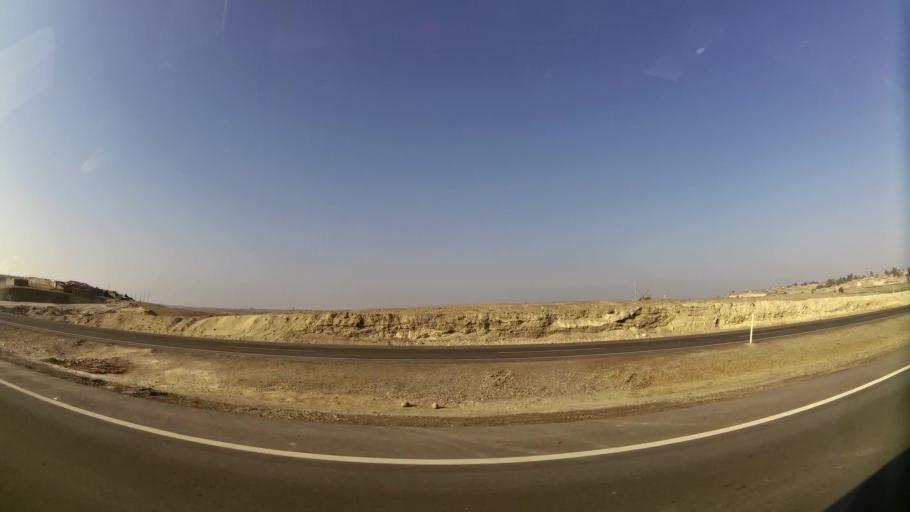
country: PE
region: Ica
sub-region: Provincia de Pisco
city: San Clemente
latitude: -13.6675
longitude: -76.1704
